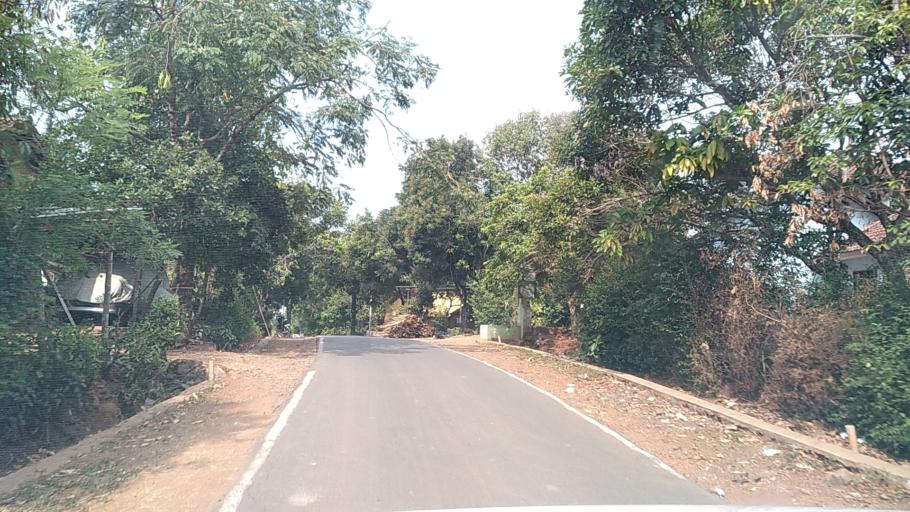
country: ID
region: Central Java
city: Ungaran
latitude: -7.0599
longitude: 110.3014
